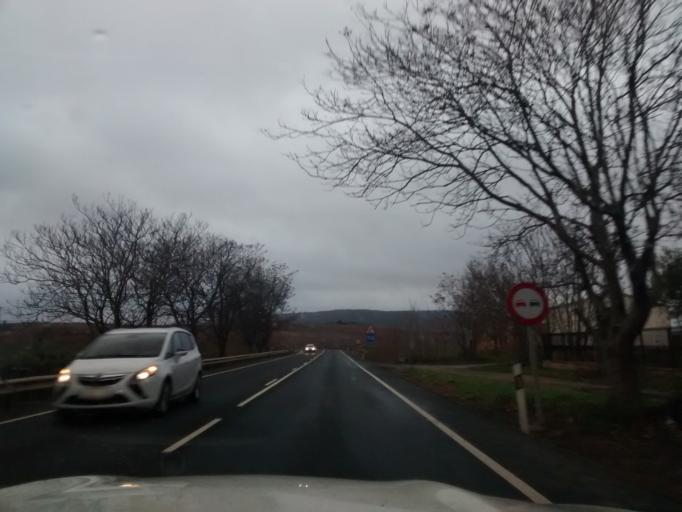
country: ES
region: La Rioja
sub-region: Provincia de La Rioja
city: Fuenmayor
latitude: 42.4598
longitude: -2.5764
